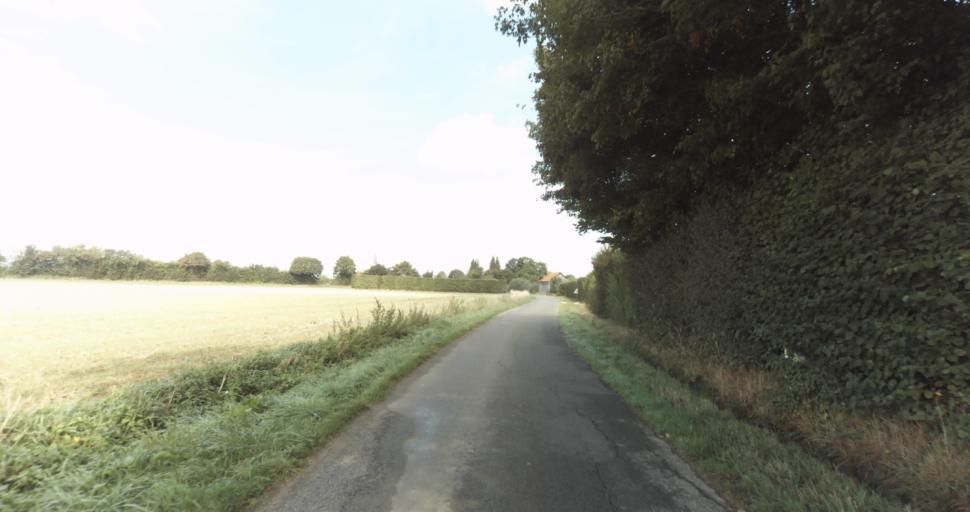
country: FR
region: Lower Normandy
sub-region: Departement du Calvados
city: Orbec
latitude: 48.9383
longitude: 0.3806
